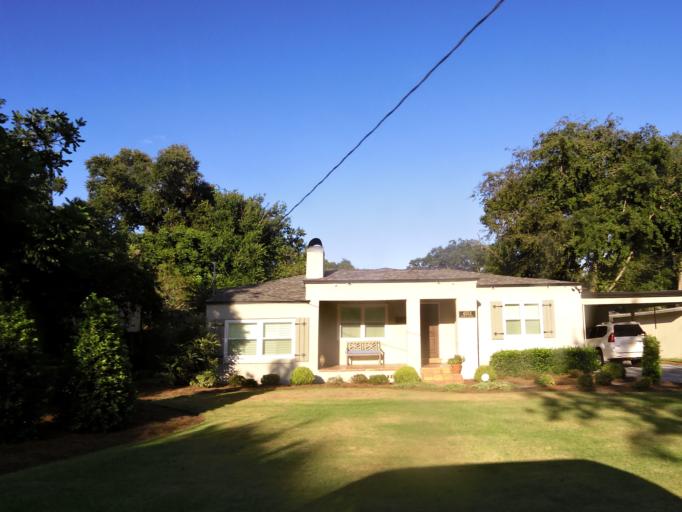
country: US
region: Florida
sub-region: Duval County
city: Jacksonville
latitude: 30.2734
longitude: -81.6480
